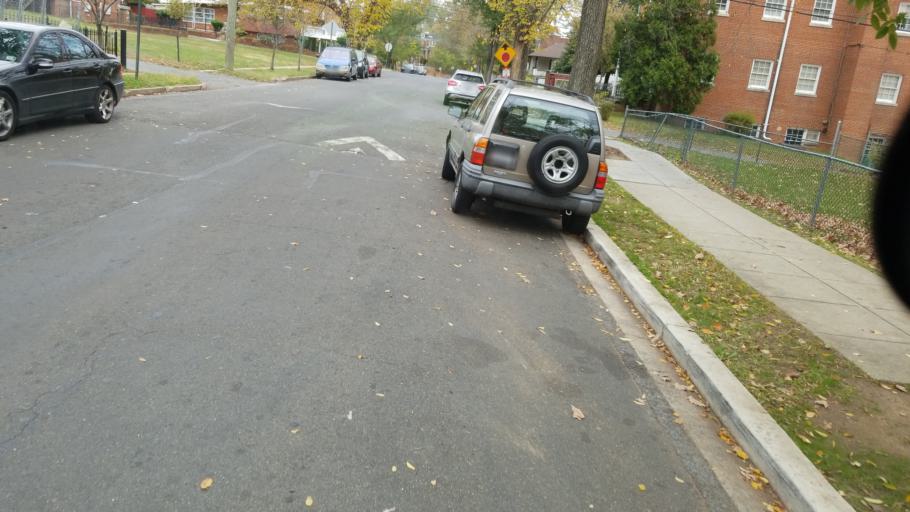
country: US
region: Maryland
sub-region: Prince George's County
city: Capitol Heights
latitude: 38.8900
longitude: -76.9260
